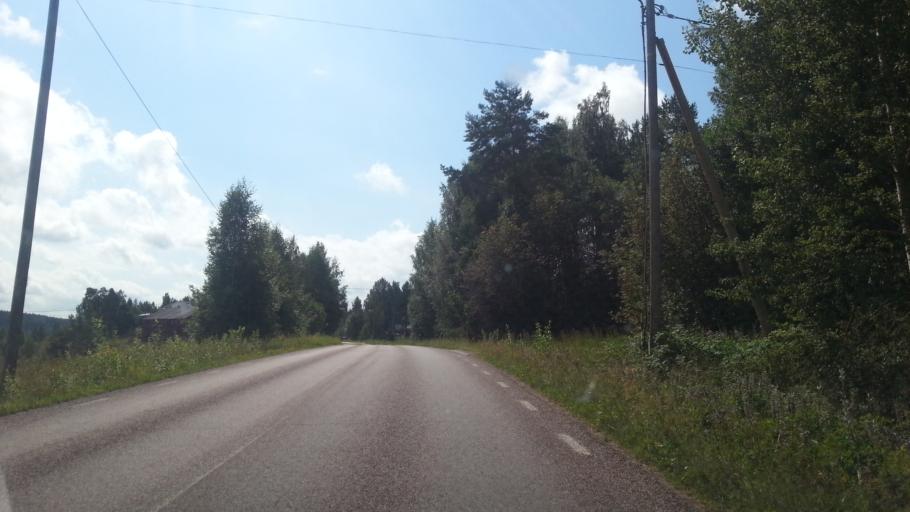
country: SE
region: Dalarna
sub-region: Faluns Kommun
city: Falun
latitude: 60.6239
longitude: 15.7675
